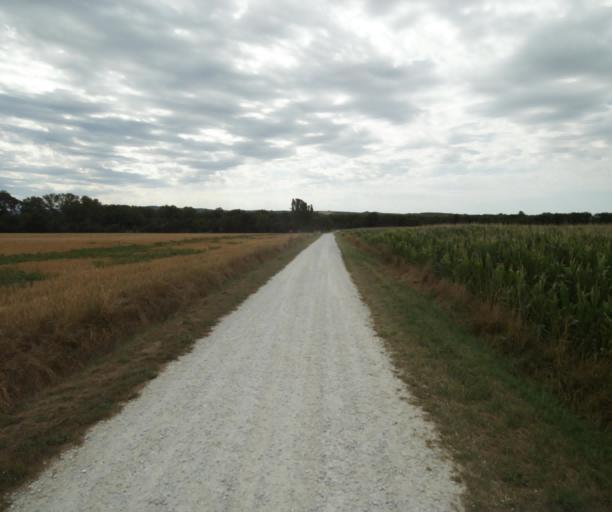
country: FR
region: Midi-Pyrenees
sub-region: Departement de la Haute-Garonne
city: Revel
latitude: 43.4330
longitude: 1.9490
